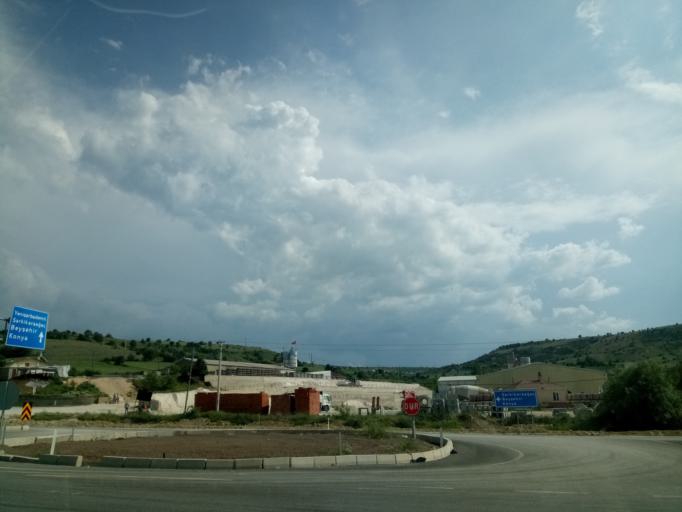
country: TR
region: Isparta
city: Bagkonak
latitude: 38.1771
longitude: 31.2603
